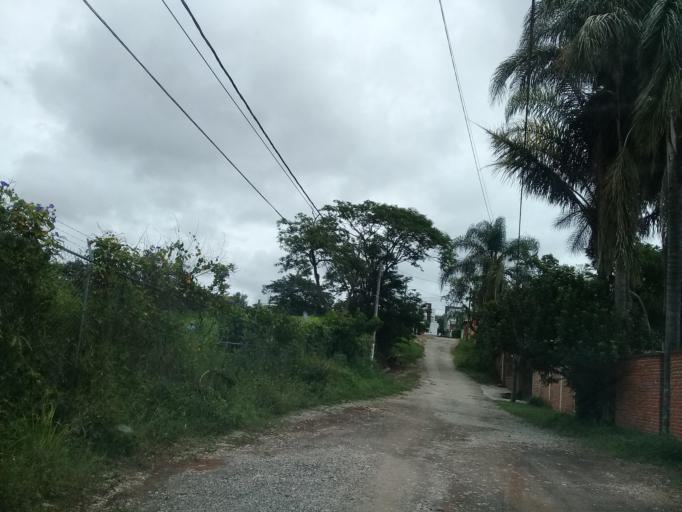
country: MX
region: Veracruz
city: El Castillo
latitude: 19.5271
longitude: -96.8788
